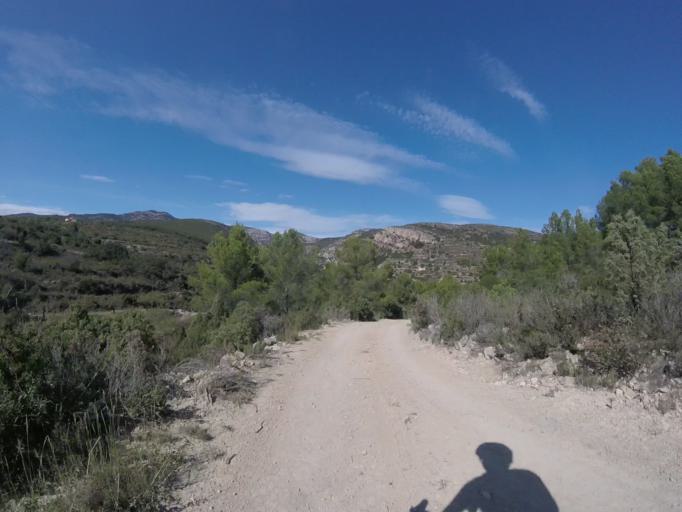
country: ES
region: Valencia
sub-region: Provincia de Castello
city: Sarratella
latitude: 40.2728
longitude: 0.0320
